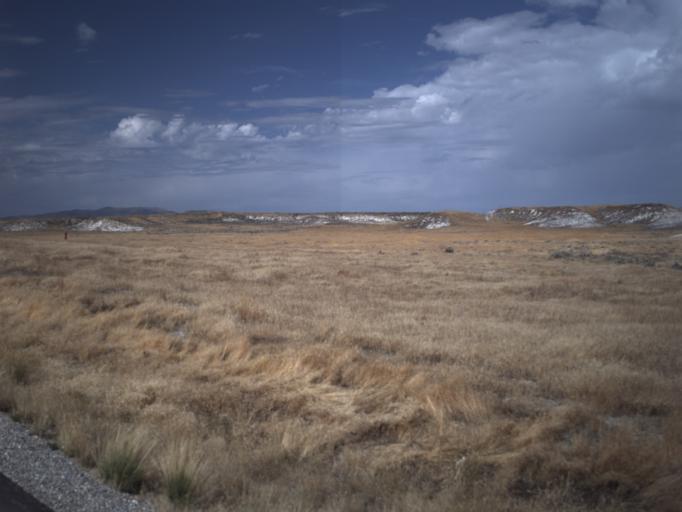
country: US
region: Utah
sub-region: Tooele County
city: Wendover
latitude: 41.3744
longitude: -114.0171
